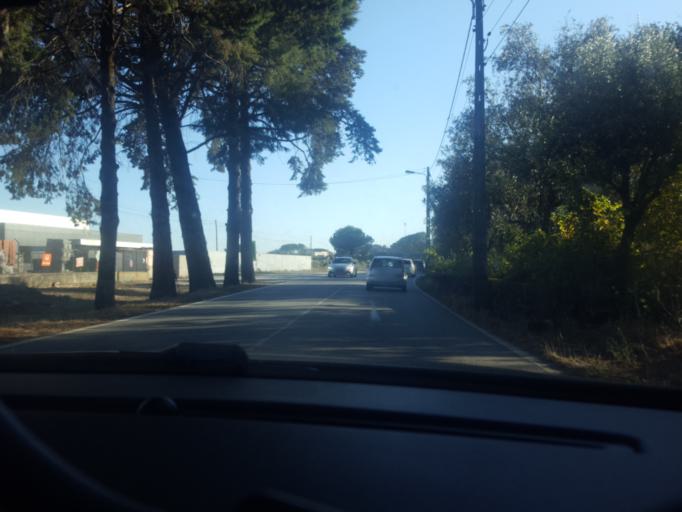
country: PT
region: Viseu
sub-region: Nelas
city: Nelas
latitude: 40.5446
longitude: -7.8431
